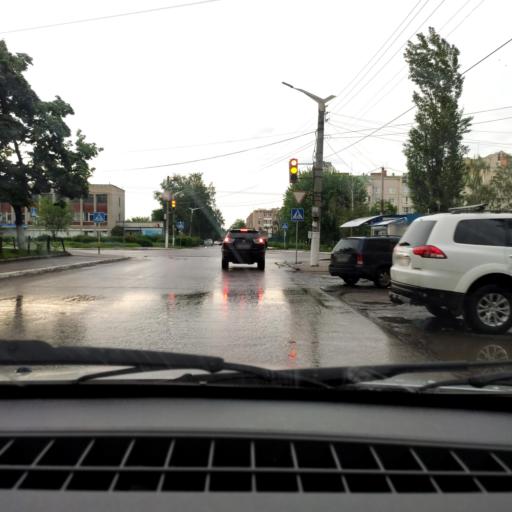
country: RU
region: Voronezj
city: Semiluki
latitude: 51.6951
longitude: 39.0183
